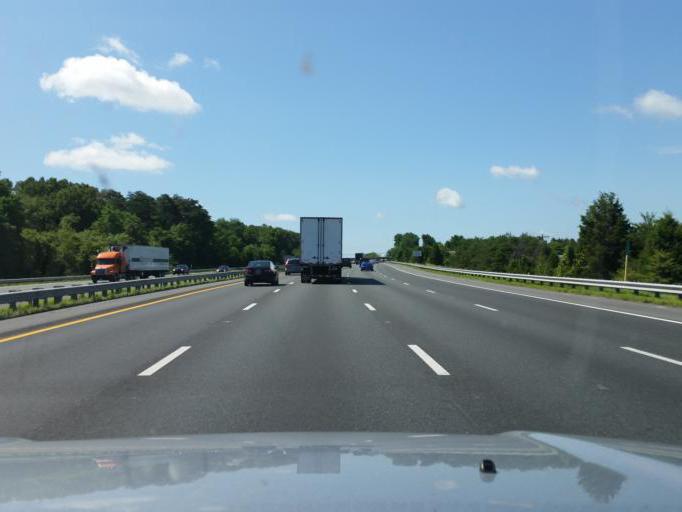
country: US
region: Virginia
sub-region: City of Fredericksburg
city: Fredericksburg
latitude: 38.2321
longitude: -77.4984
